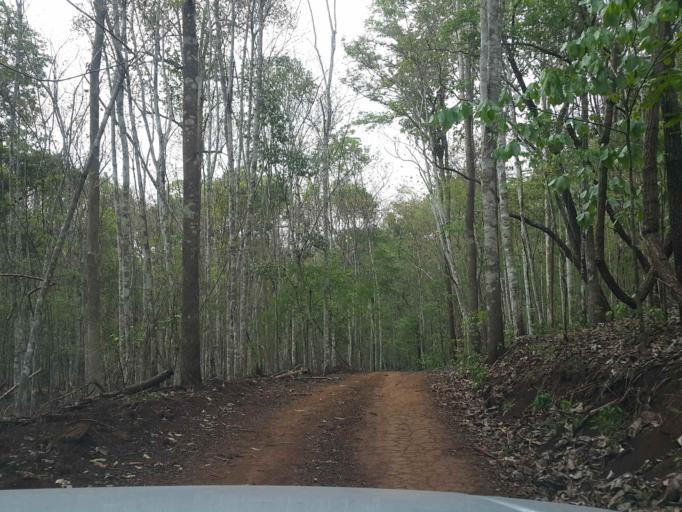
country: TH
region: Chiang Mai
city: Wiang Haeng
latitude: 19.3338
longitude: 98.7184
